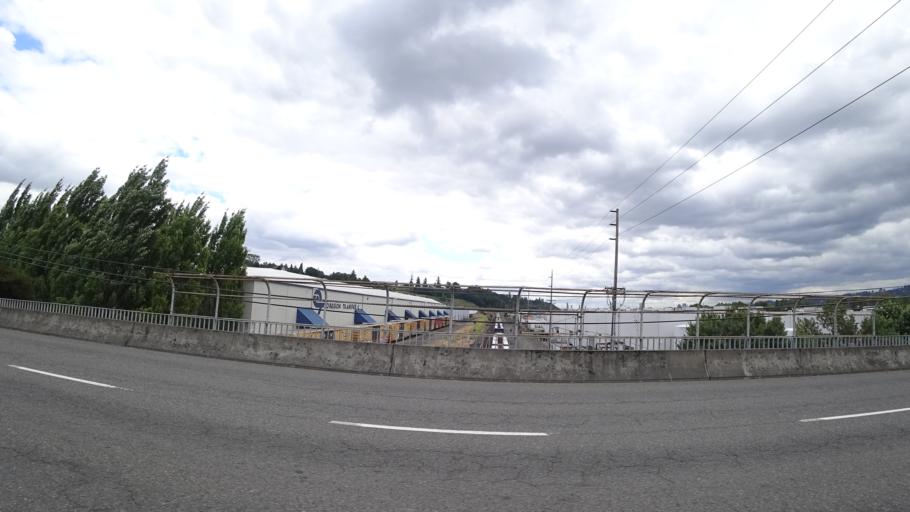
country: US
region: Oregon
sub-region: Multnomah County
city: Portland
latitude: 45.5677
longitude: -122.7072
